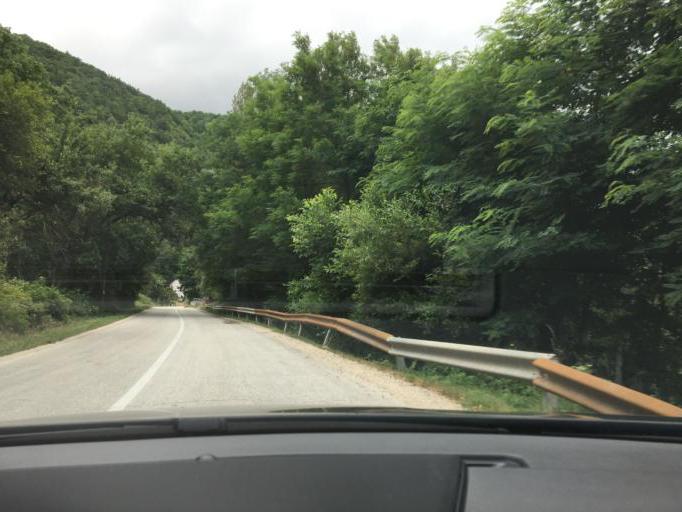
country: MK
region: Kriva Palanka
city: Kriva Palanka
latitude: 42.2260
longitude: 22.3585
